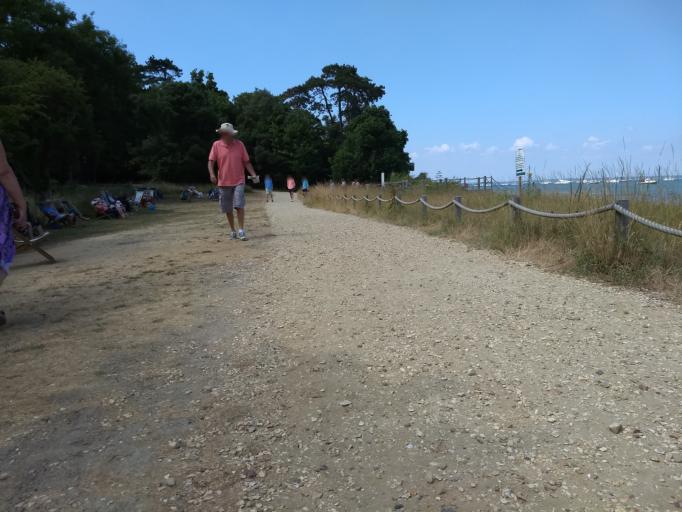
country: GB
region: England
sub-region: Isle of Wight
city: East Cowes
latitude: 50.7556
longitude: -1.2574
